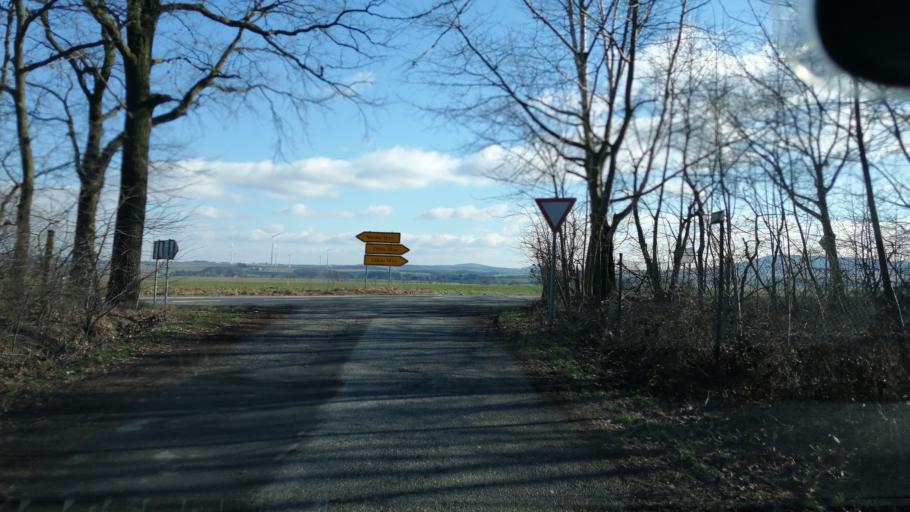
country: DE
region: Saxony
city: Weissenberg
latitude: 51.1599
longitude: 14.7215
